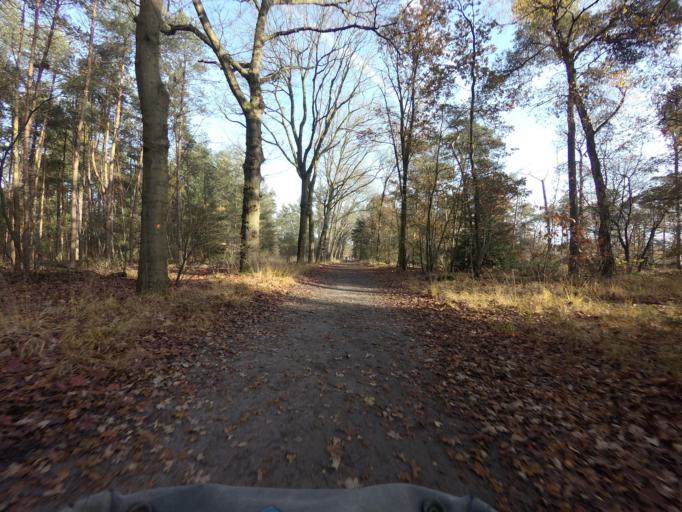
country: NL
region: North Brabant
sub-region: Gemeente Breda
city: Breda
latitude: 51.5493
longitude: 4.7673
